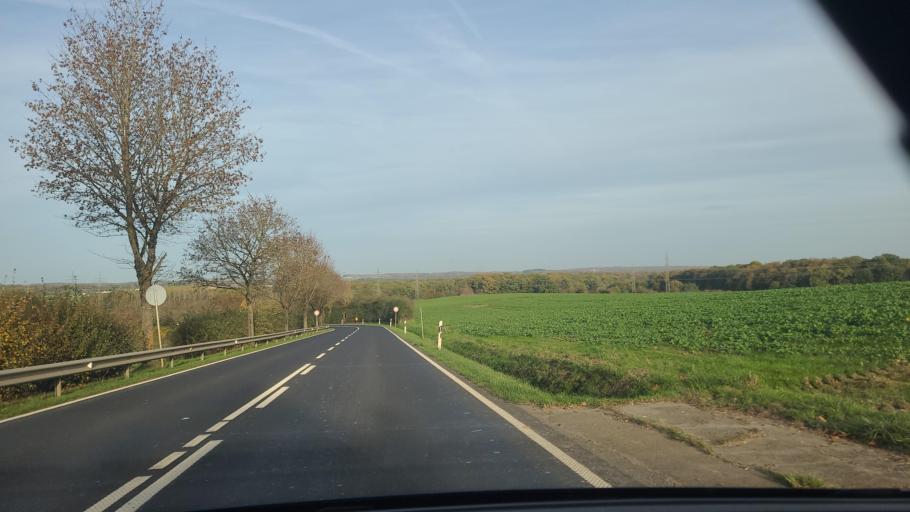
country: LU
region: Luxembourg
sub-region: Canton de Capellen
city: Garnich
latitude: 49.6268
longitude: 5.9539
